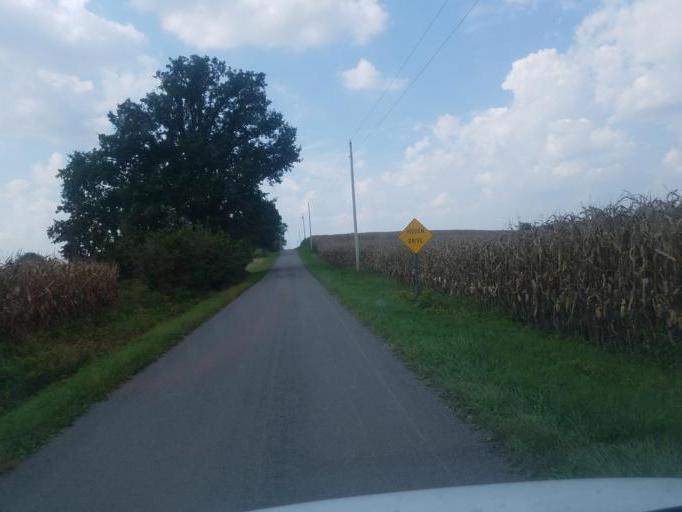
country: US
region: Ohio
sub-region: Hardin County
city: Ada
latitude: 40.6377
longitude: -83.8675
